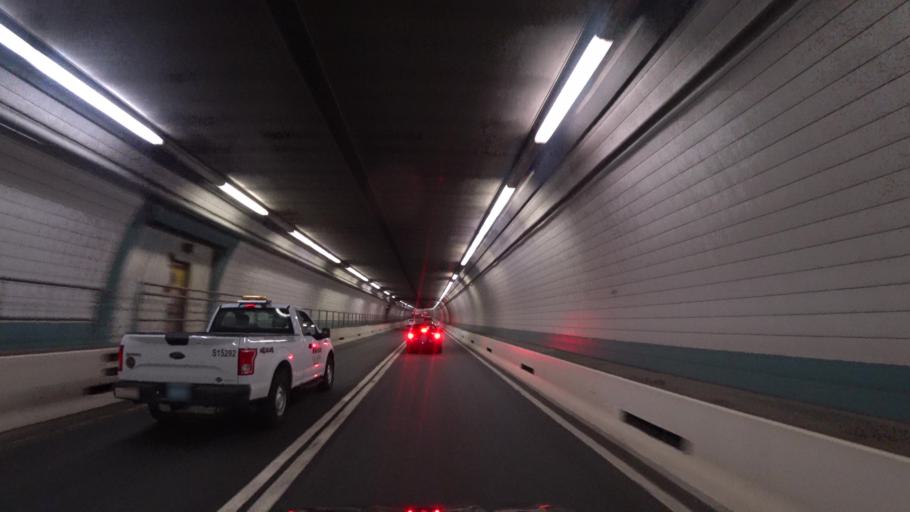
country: US
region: Massachusetts
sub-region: Suffolk County
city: South Boston
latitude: 42.3555
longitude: -71.0294
